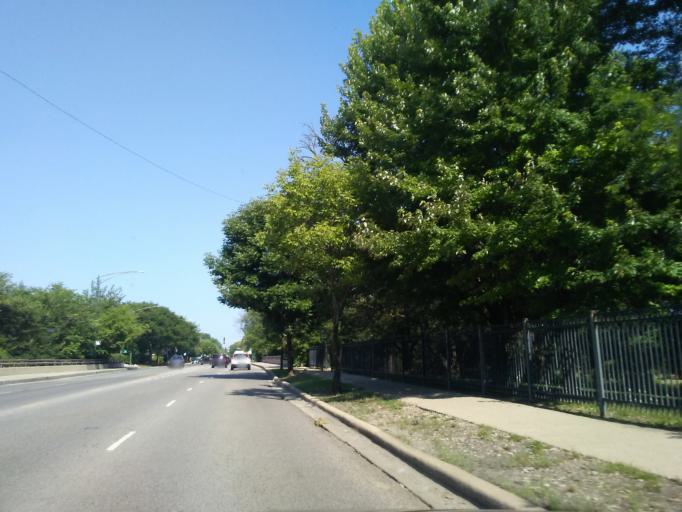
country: US
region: Illinois
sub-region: Cook County
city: Lincolnwood
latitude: 41.9755
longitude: -87.7316
